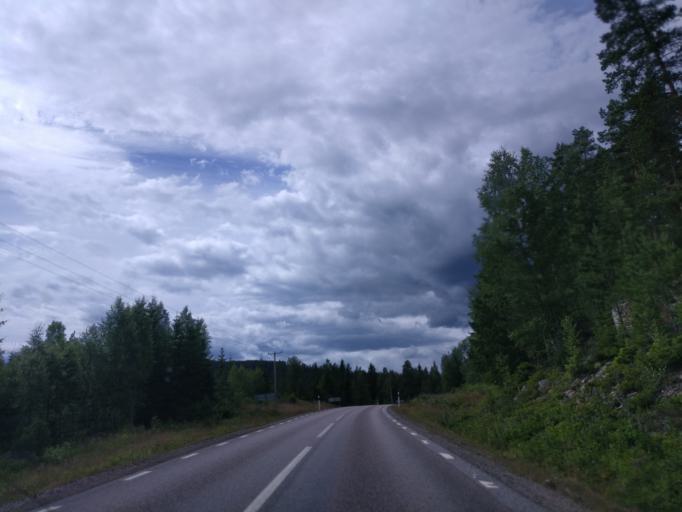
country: SE
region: Vaermland
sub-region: Hagfors Kommun
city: Ekshaerad
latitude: 60.1802
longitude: 13.3628
